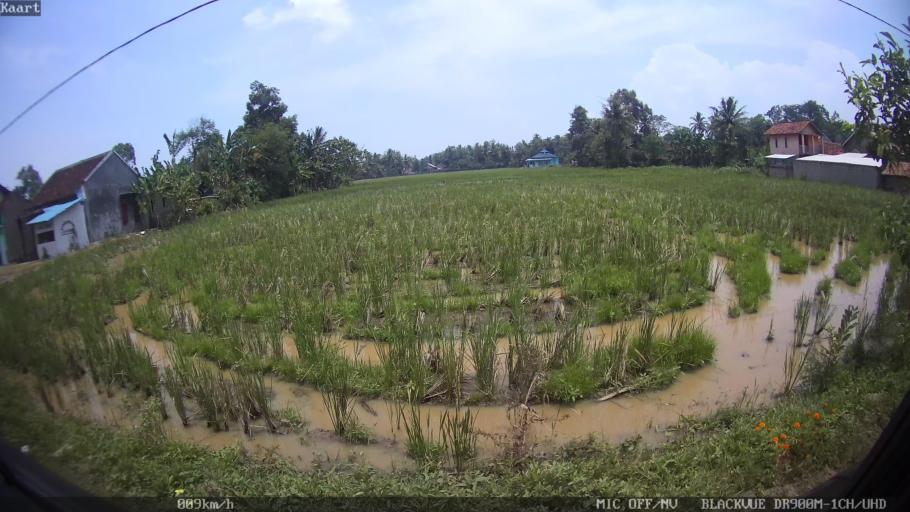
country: ID
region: Lampung
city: Natar
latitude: -5.3152
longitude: 105.2394
